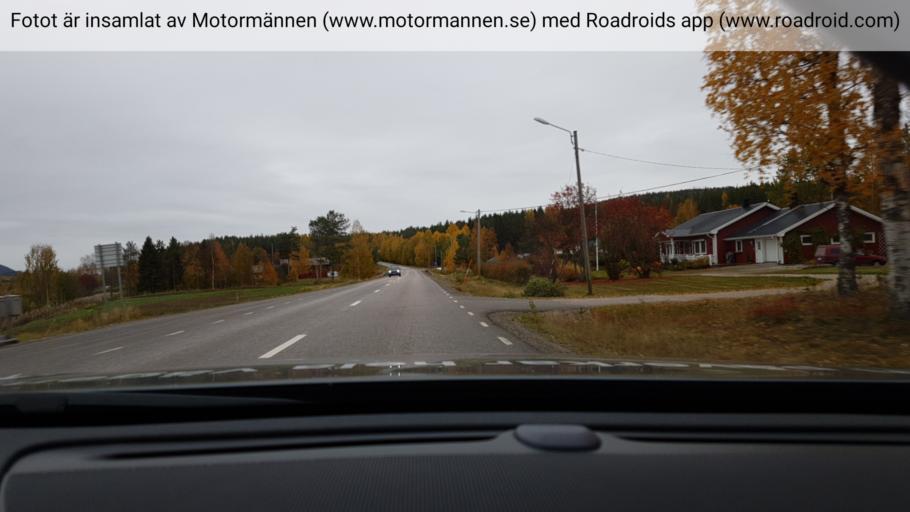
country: SE
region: Norrbotten
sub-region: Overkalix Kommun
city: OEverkalix
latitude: 66.5105
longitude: 22.7648
